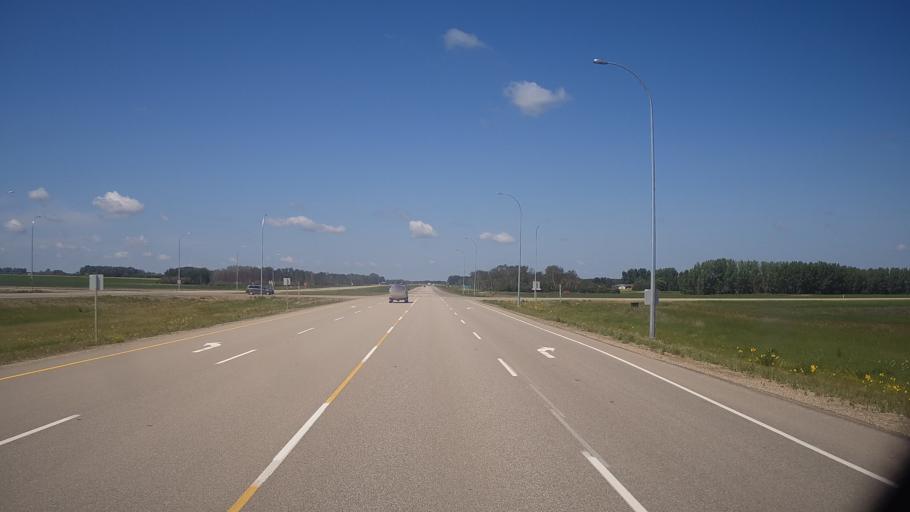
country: CA
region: Saskatchewan
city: Saskatoon
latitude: 52.0123
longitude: -106.3831
